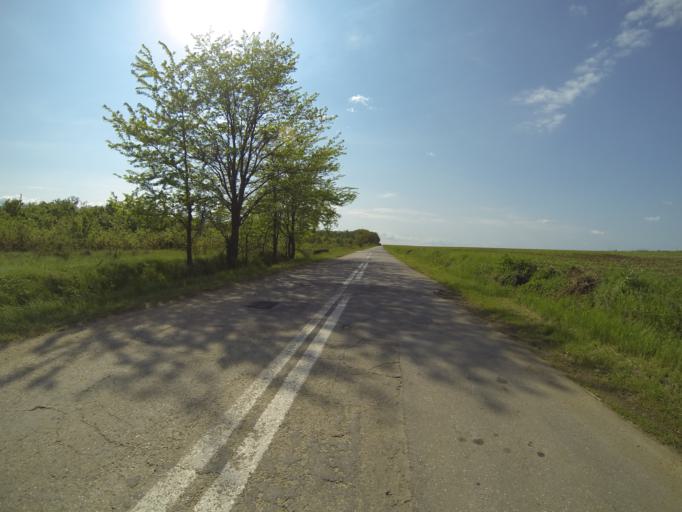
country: RO
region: Dolj
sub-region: Comuna Plenita
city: Castrele Traiane
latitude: 44.2538
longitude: 23.1513
